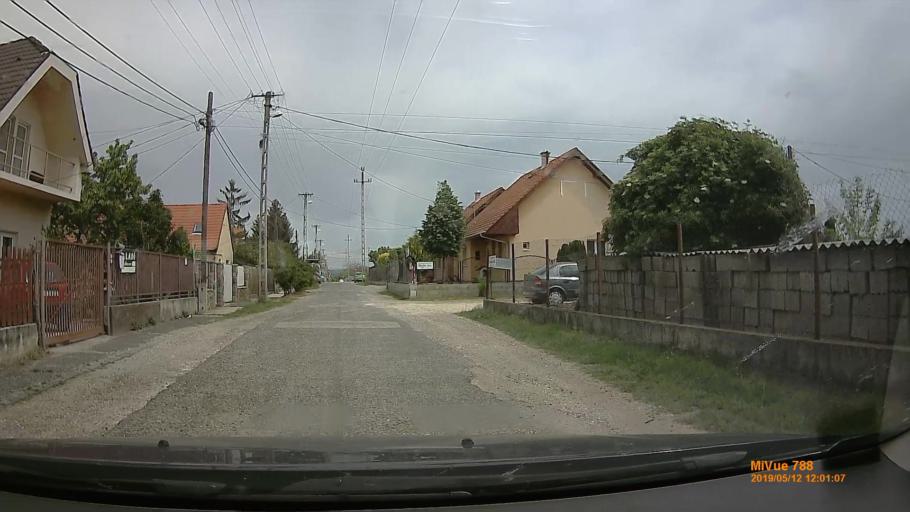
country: HU
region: Budapest
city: Budapest XVII. keruelet
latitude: 47.4692
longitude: 19.2596
